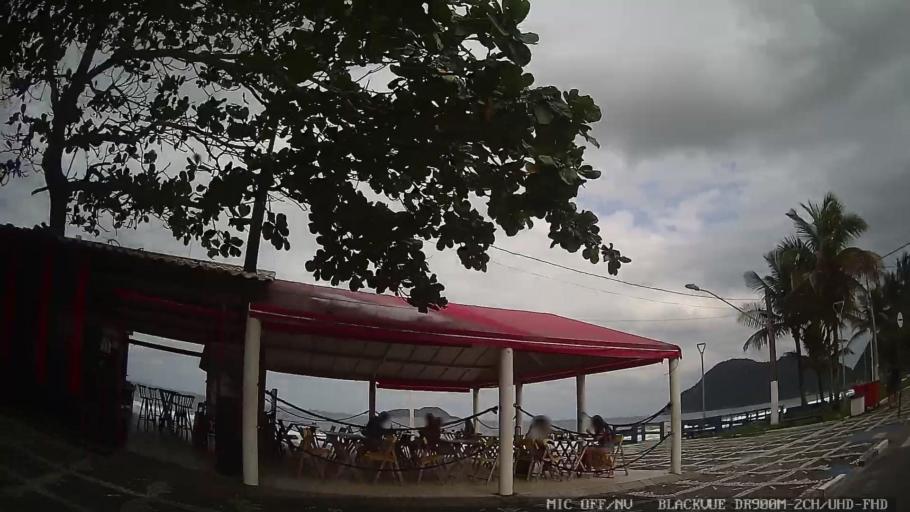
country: BR
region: Sao Paulo
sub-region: Guaruja
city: Guaruja
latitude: -24.0133
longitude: -46.2722
